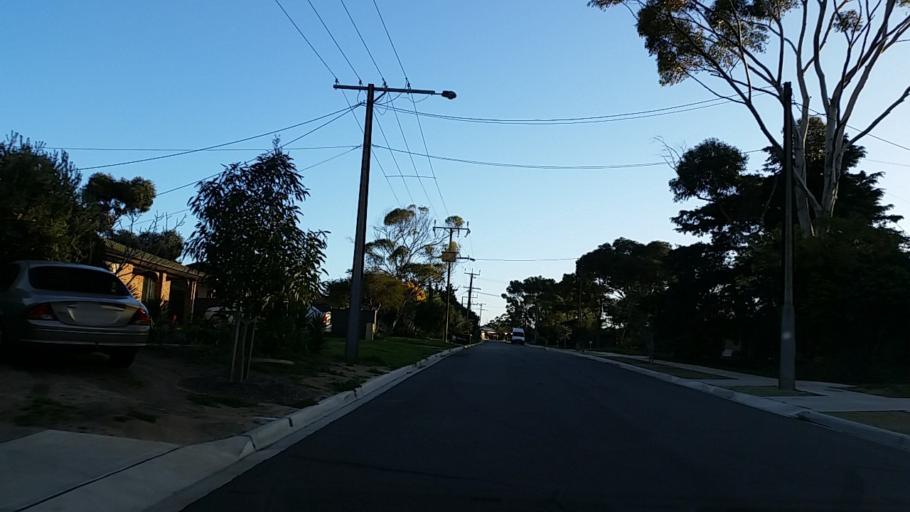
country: AU
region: South Australia
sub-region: Onkaparinga
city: Morphett Vale
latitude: -35.1346
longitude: 138.5297
